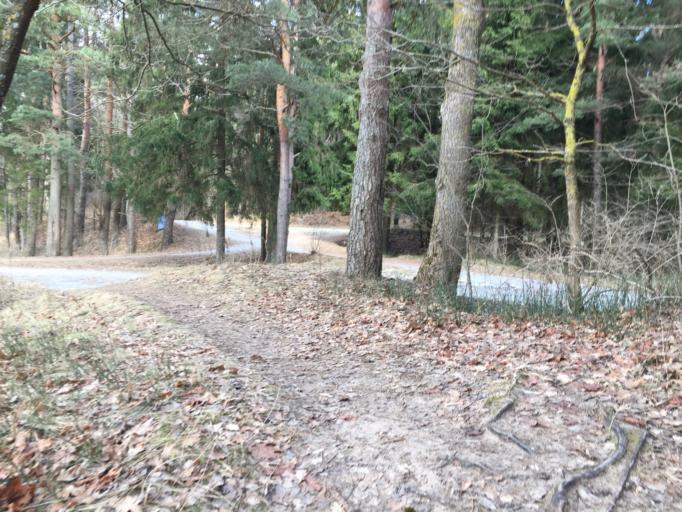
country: LV
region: Valmieras Rajons
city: Valmiera
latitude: 57.5353
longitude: 25.4369
